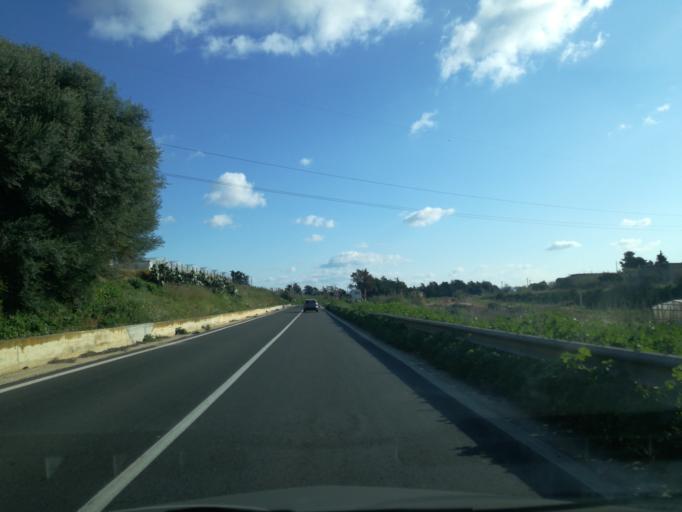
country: IT
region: Sicily
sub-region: Ragusa
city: Acate
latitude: 36.9939
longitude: 14.4339
